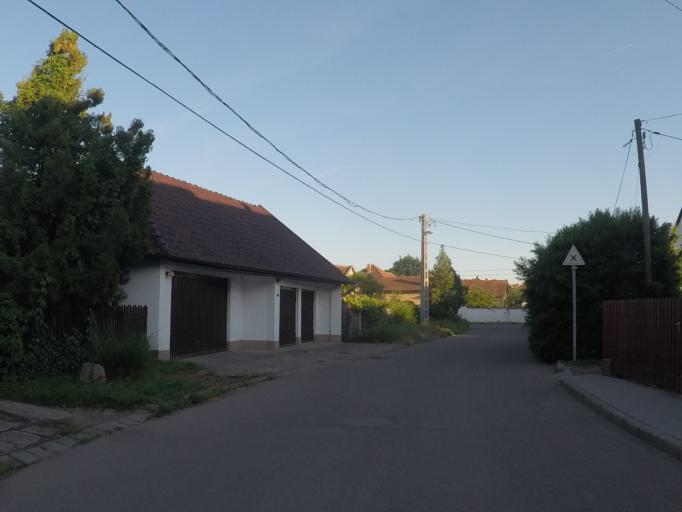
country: HU
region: Heves
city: Heves
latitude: 47.5928
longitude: 20.2856
